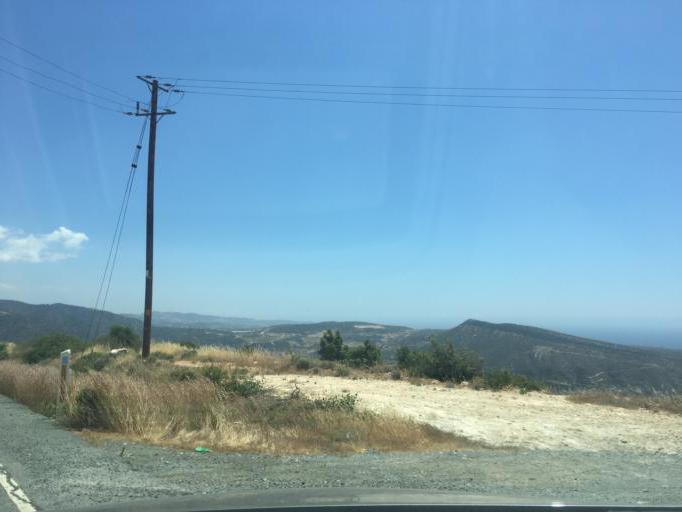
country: CY
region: Limassol
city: Mouttagiaka
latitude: 34.7574
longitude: 33.0628
